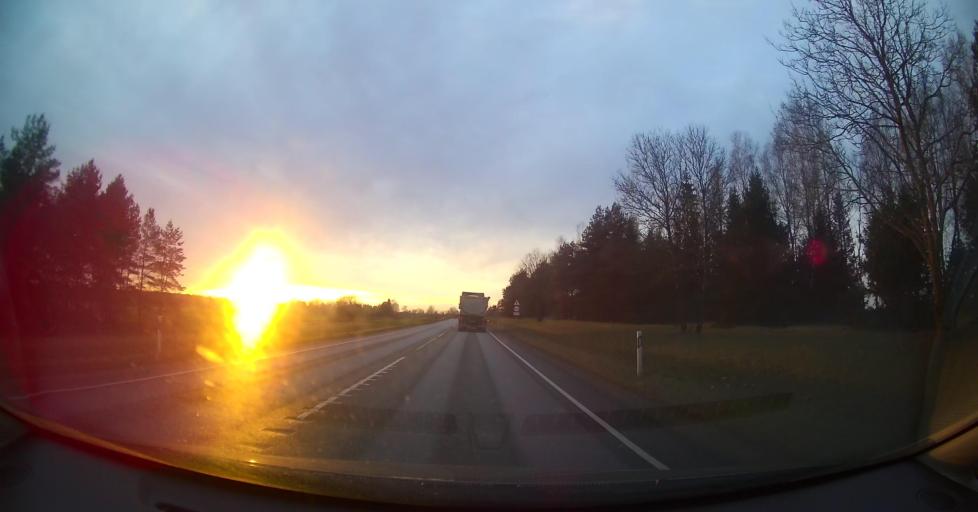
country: EE
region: Ida-Virumaa
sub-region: Aseri vald
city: Aseri
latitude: 59.4359
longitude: 26.7190
